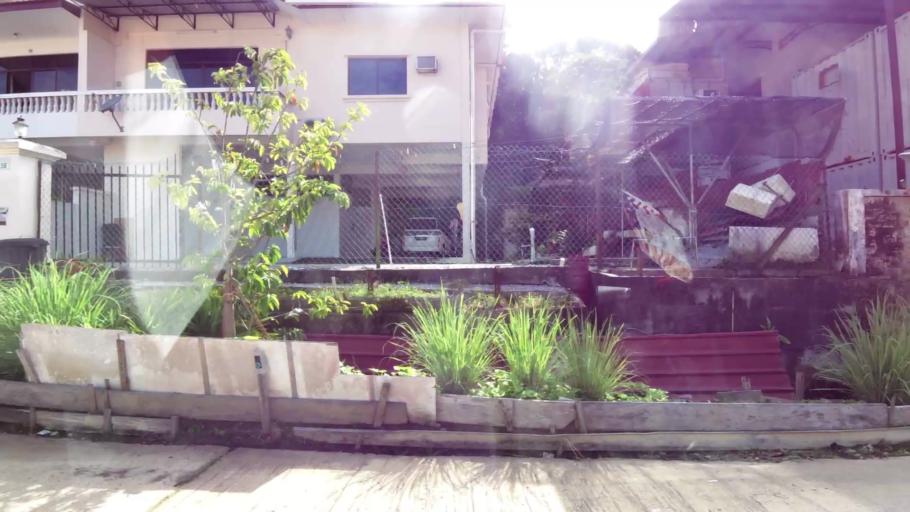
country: BN
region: Brunei and Muara
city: Bandar Seri Begawan
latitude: 4.9030
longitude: 114.9701
